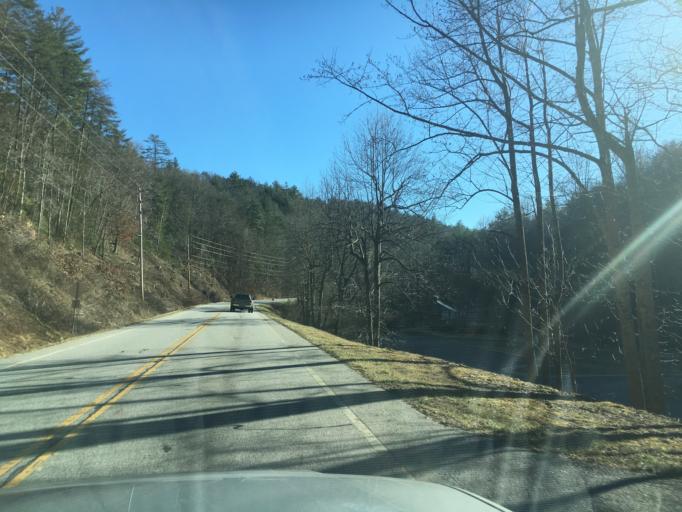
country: US
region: Georgia
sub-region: Union County
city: Blairsville
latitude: 34.7806
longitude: -83.9095
